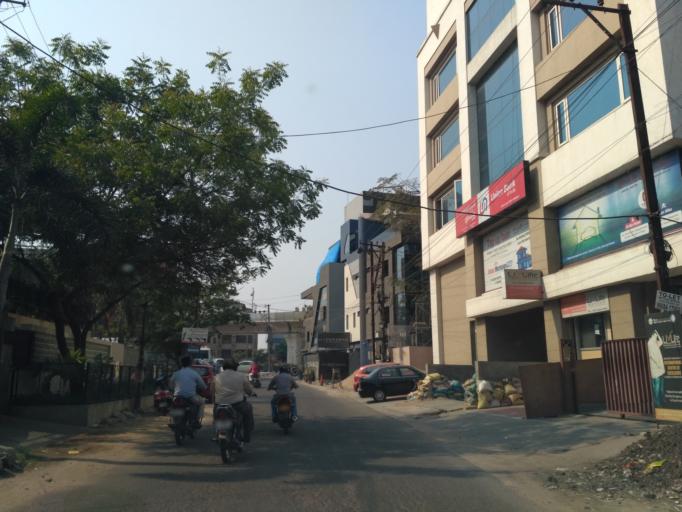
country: IN
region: Telangana
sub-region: Rangareddi
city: Kukatpalli
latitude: 17.4379
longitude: 78.3994
